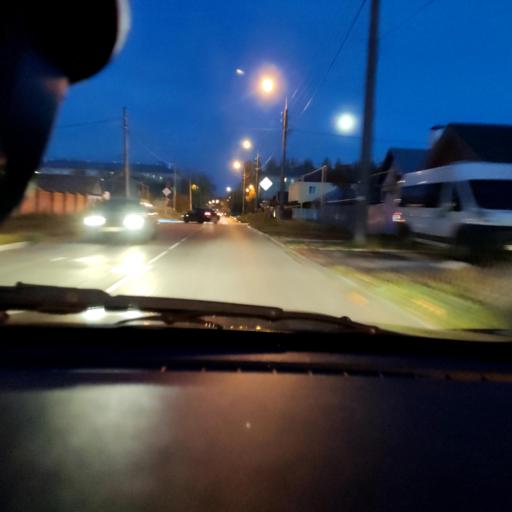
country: RU
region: Samara
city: Tol'yatti
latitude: 53.5260
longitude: 49.4256
